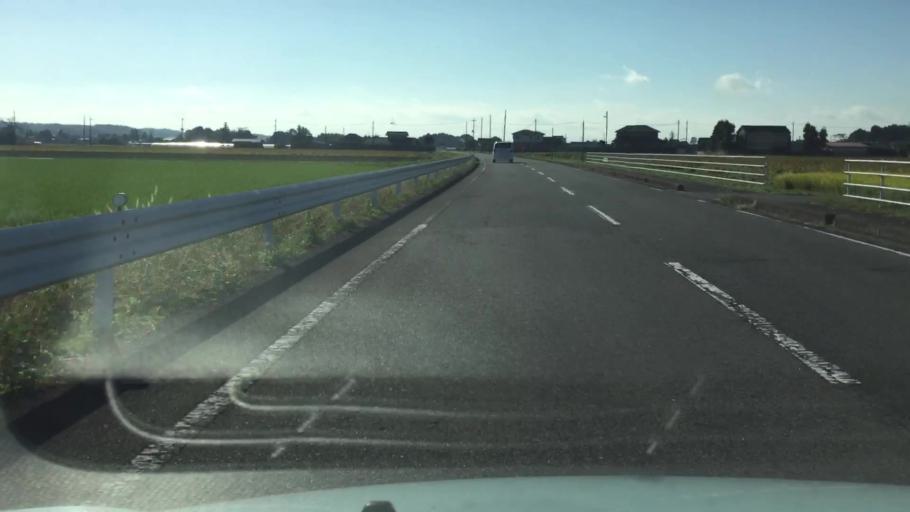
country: JP
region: Tochigi
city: Ujiie
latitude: 36.6738
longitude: 140.0147
